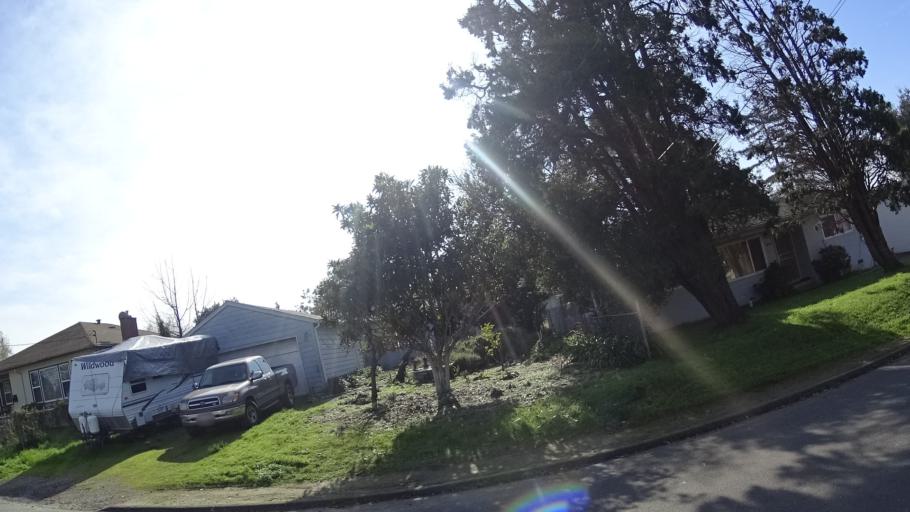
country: US
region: California
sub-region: Alameda County
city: Fairview
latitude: 37.6746
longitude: -122.0634
